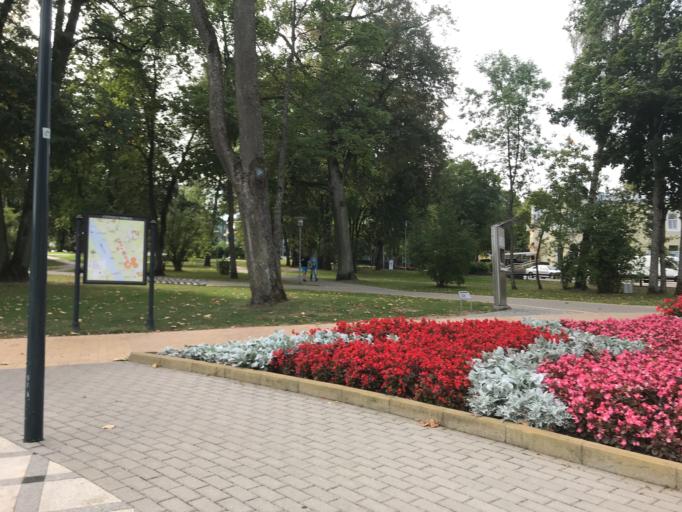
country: LT
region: Alytaus apskritis
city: Druskininkai
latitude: 54.0209
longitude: 23.9747
